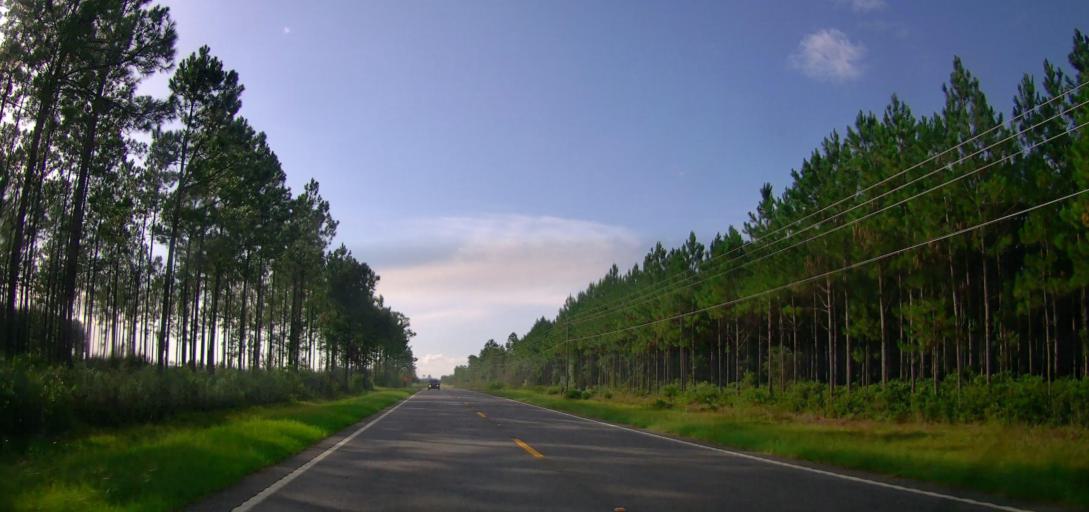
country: US
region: Georgia
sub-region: Coffee County
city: Nicholls
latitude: 31.3642
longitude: -82.6269
